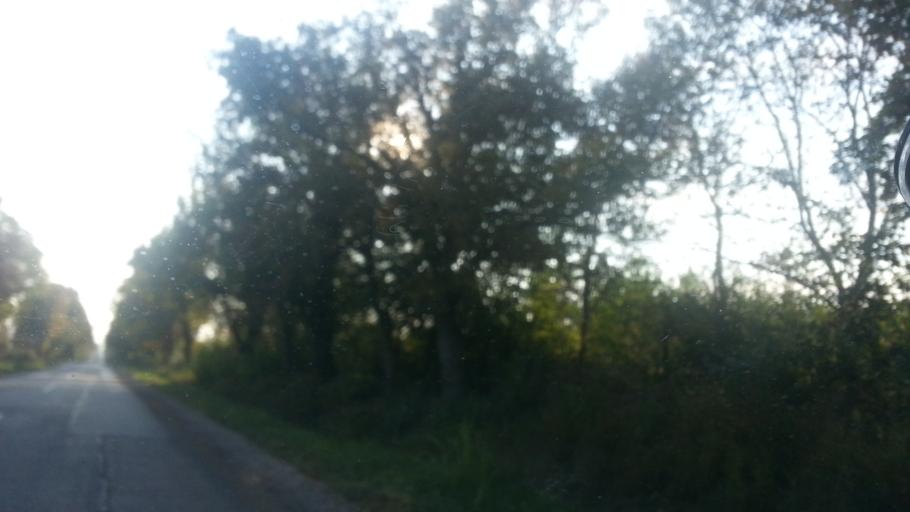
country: RS
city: Novi Slankamen
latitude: 45.1124
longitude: 20.2214
